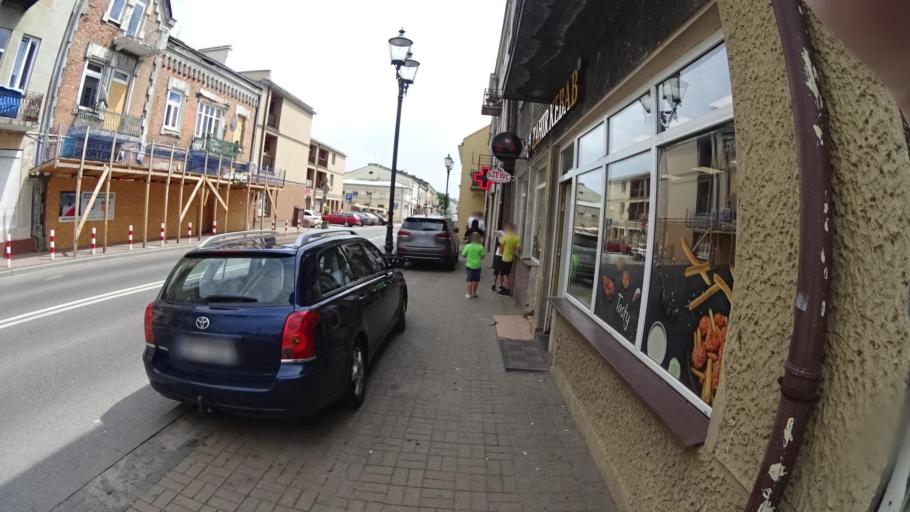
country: PL
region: Masovian Voivodeship
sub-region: Powiat grojecki
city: Grojec
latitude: 51.8675
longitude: 20.8657
